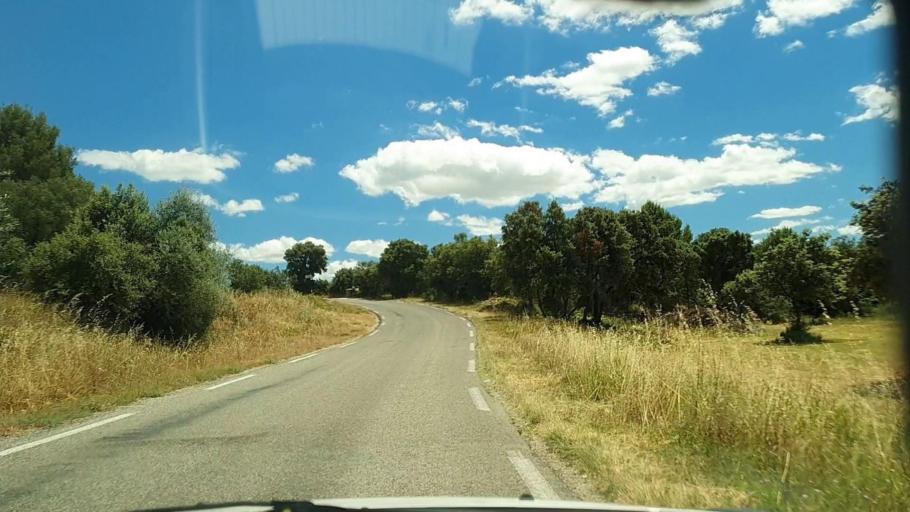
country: FR
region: Languedoc-Roussillon
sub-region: Departement du Gard
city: Cabrieres
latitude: 43.9105
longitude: 4.4561
